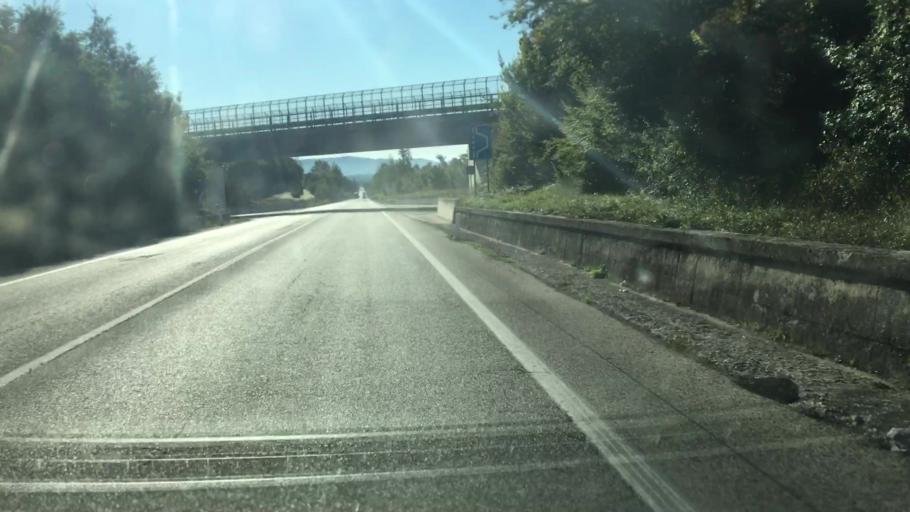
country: IT
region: Molise
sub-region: Provincia di Campobasso
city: Vinchiaturo
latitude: 41.4526
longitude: 14.5859
